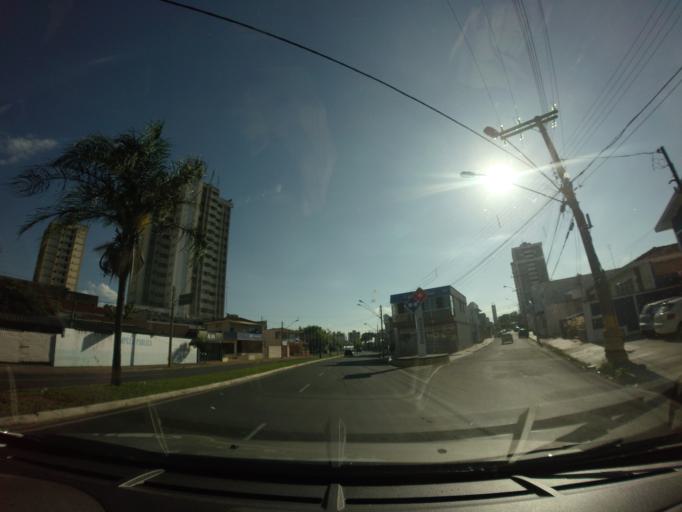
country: BR
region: Sao Paulo
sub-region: Rio Claro
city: Rio Claro
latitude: -22.4114
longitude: -47.5679
